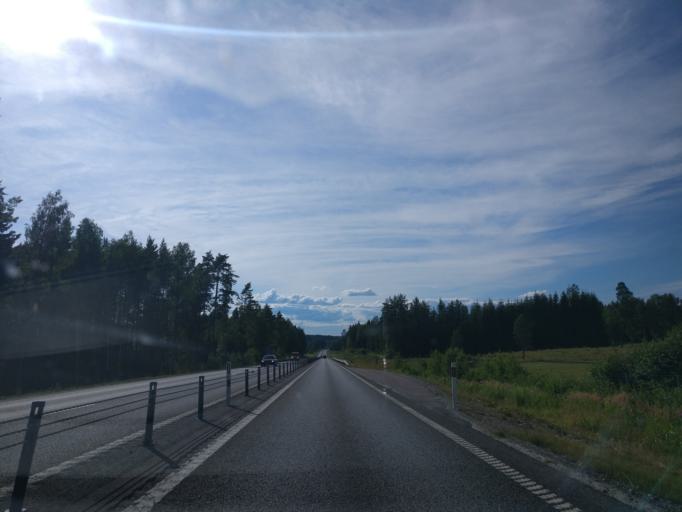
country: SE
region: Vaermland
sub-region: Arvika Kommun
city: Arvika
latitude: 59.6503
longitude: 12.6778
